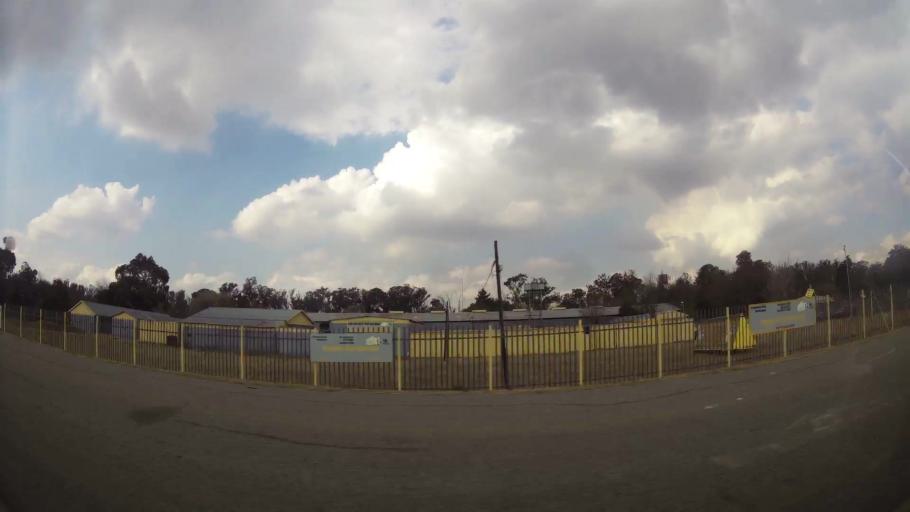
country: ZA
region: Gauteng
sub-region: Sedibeng District Municipality
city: Vereeniging
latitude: -26.6928
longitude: 27.9391
